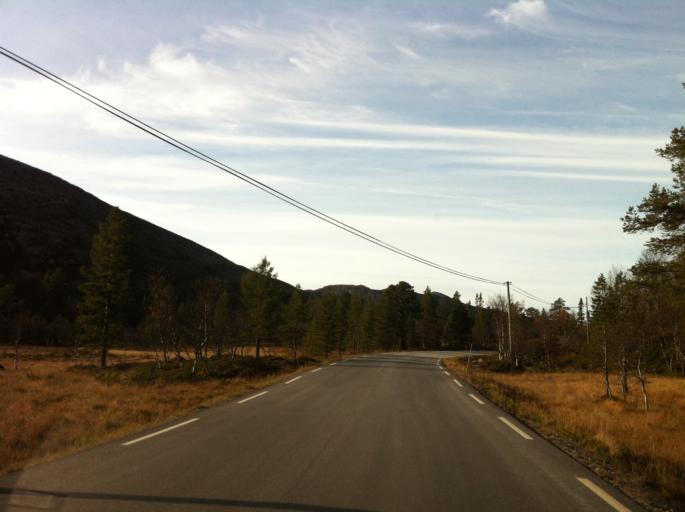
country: NO
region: Hedmark
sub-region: Engerdal
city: Engerdal
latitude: 62.0849
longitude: 12.0684
